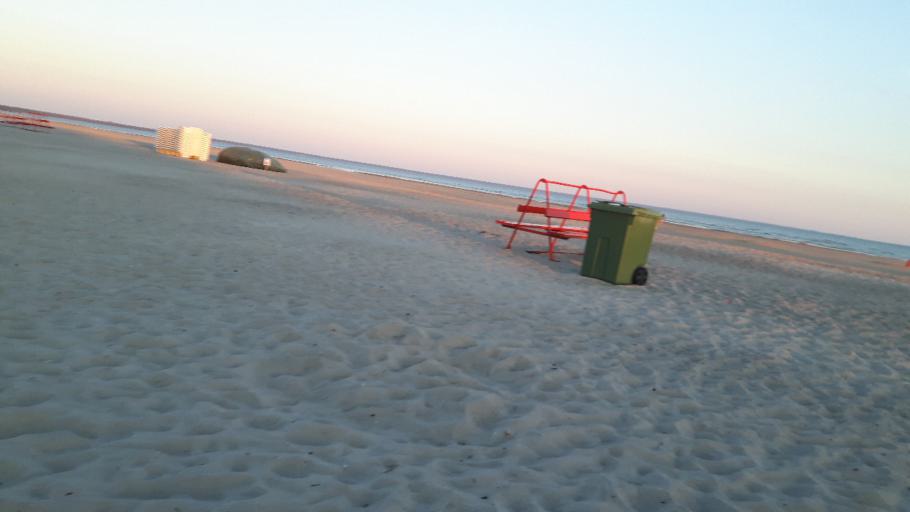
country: EE
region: Paernumaa
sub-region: Paernu linn
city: Parnu
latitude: 58.3730
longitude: 24.5004
